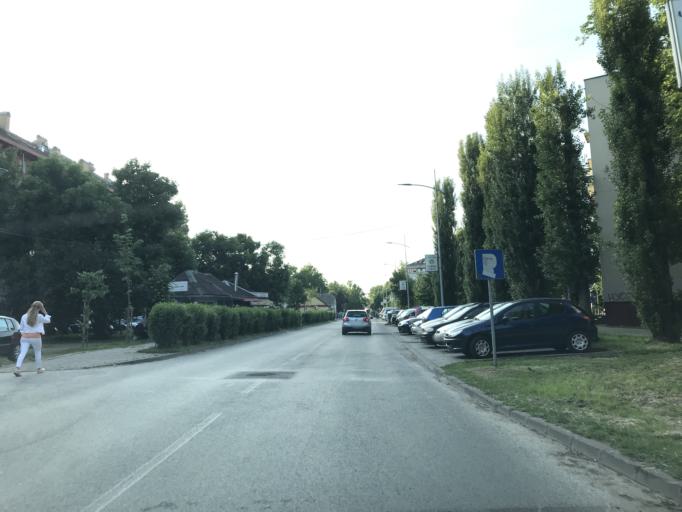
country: RS
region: Autonomna Pokrajina Vojvodina
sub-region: Juznobacki Okrug
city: Novi Sad
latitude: 45.2625
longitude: 19.8123
